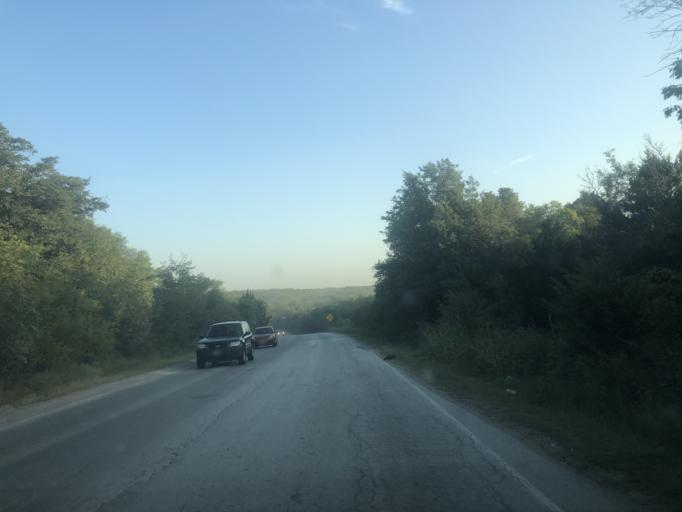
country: US
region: Texas
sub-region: Tarrant County
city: Lakeside
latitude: 32.7891
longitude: -97.4904
